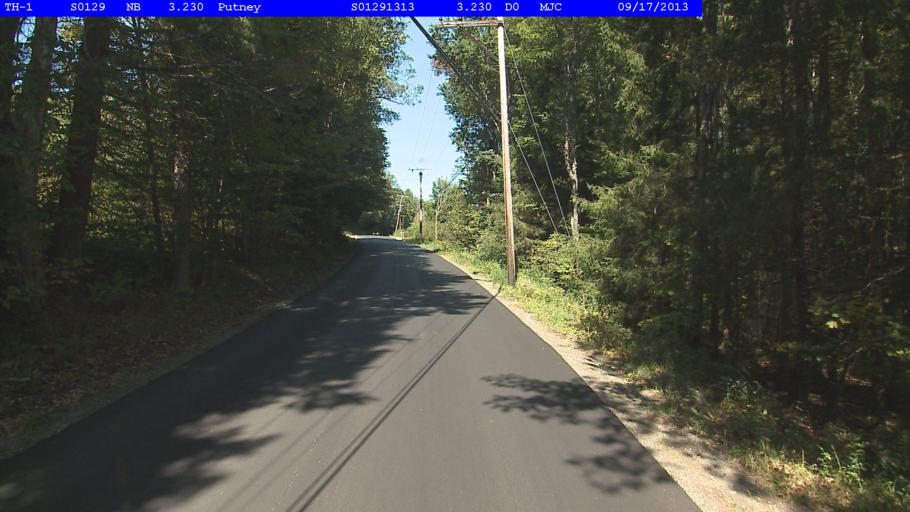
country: US
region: New Hampshire
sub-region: Cheshire County
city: Westmoreland
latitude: 43.0183
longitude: -72.5259
